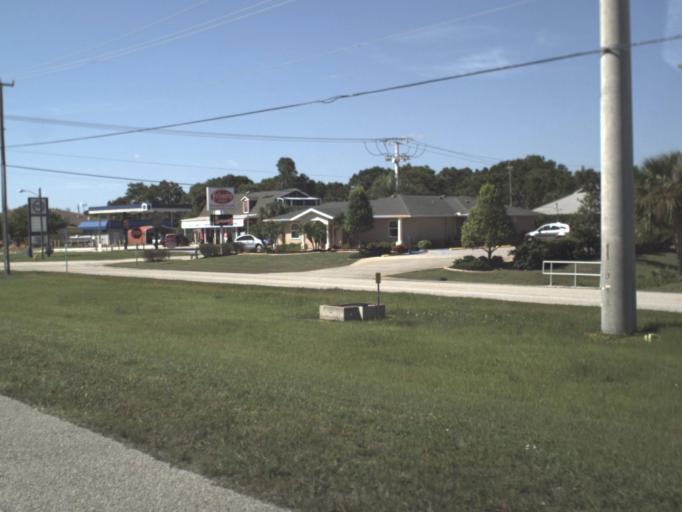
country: US
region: Florida
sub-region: Charlotte County
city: Grove City
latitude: 26.9334
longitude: -82.2876
